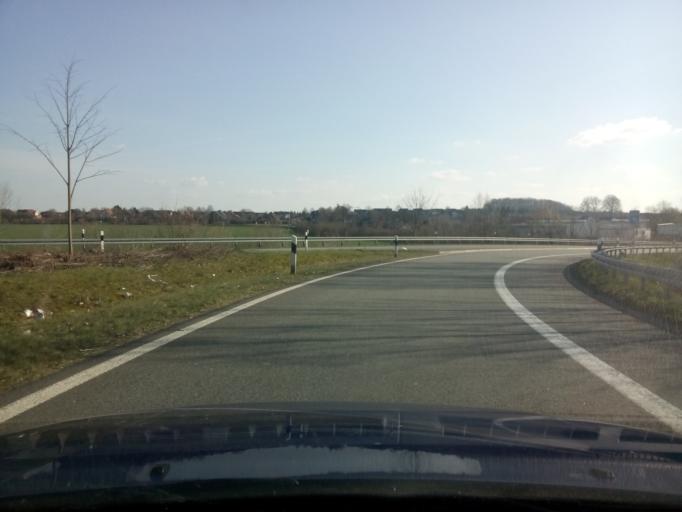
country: DE
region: Lower Saxony
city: Melle
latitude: 52.2151
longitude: 8.2762
